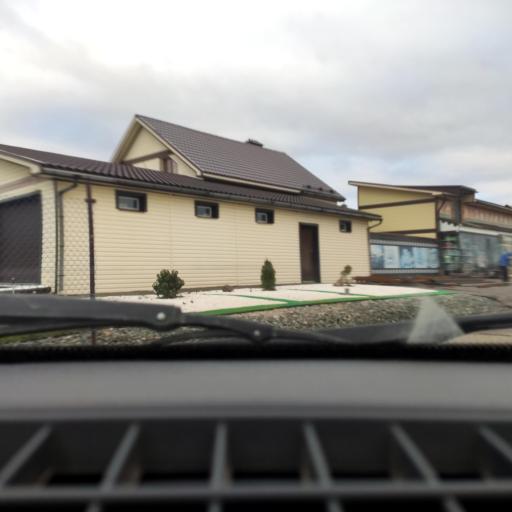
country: RU
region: Bashkortostan
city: Avdon
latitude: 54.6577
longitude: 55.7416
